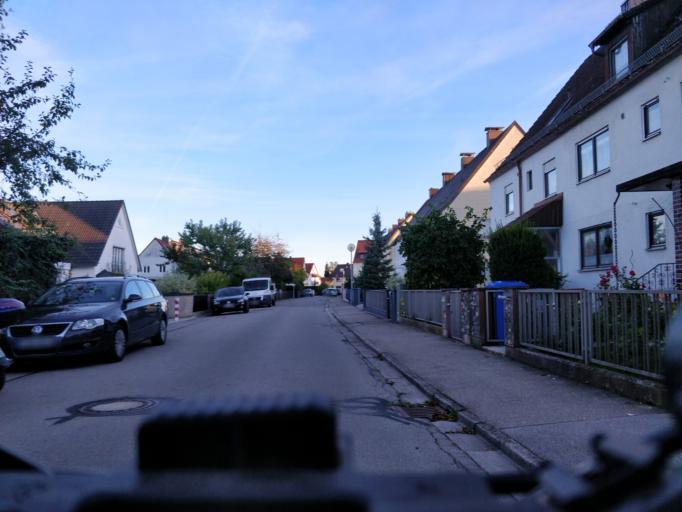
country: DE
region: Bavaria
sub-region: Swabia
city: Mering
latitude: 48.2816
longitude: 10.9701
